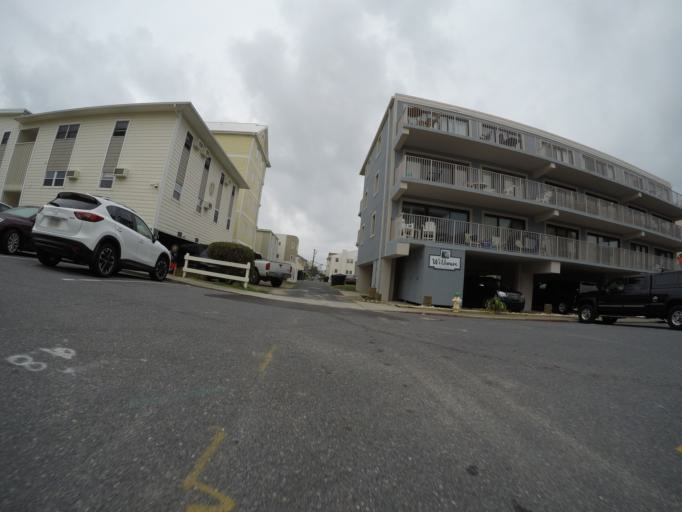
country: US
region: Maryland
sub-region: Worcester County
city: Ocean City
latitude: 38.3701
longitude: -75.0692
